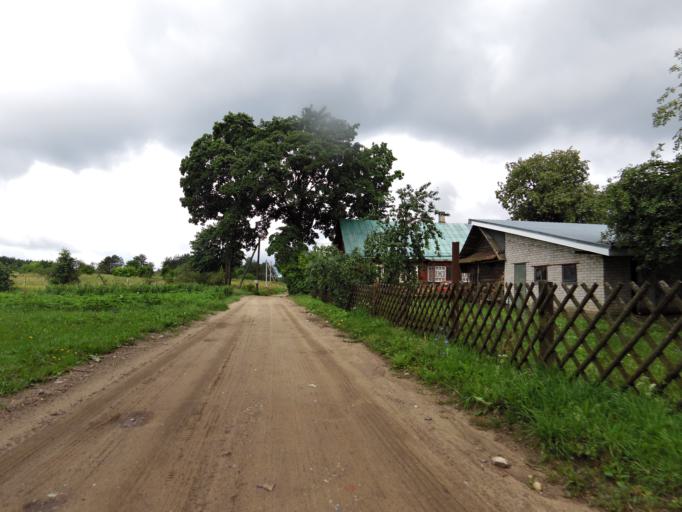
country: LT
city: Grigiskes
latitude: 54.7033
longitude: 25.1082
